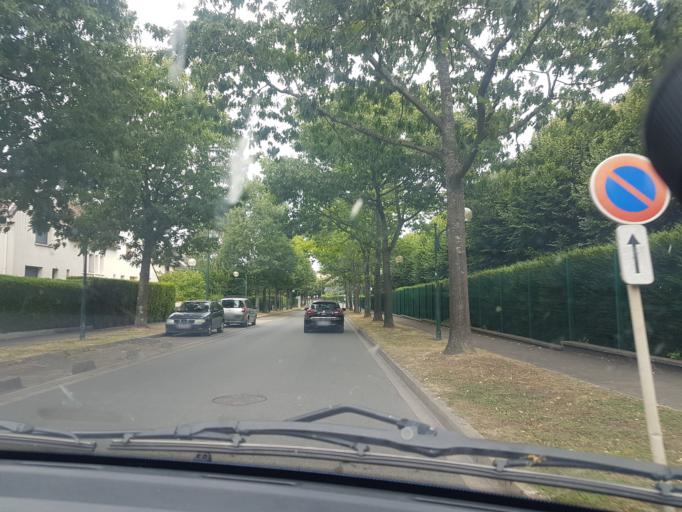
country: FR
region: Ile-de-France
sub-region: Departement des Yvelines
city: Plaisir
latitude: 48.8234
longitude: 1.9448
